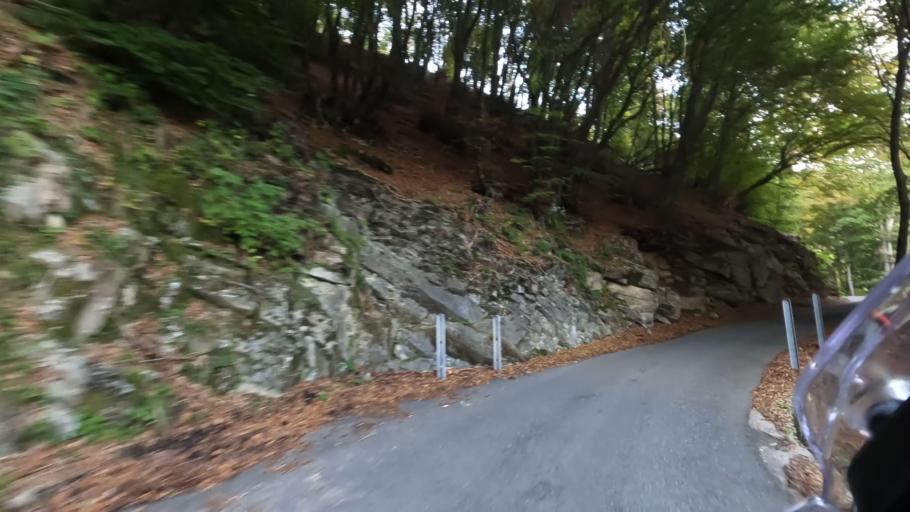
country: IT
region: Lombardy
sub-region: Provincia di Como
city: Pigra
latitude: 45.9692
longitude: 9.1196
